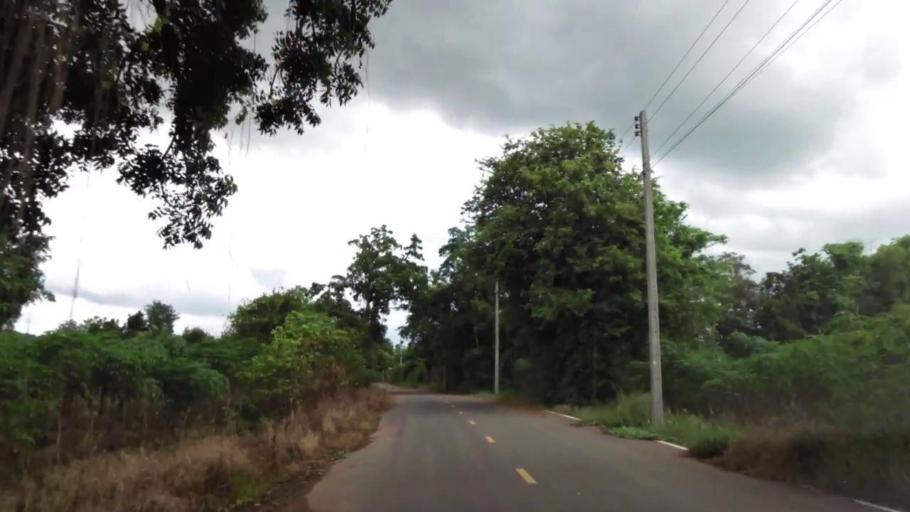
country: TH
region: Nakhon Sawan
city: Phai Sali
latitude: 15.6053
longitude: 100.6599
